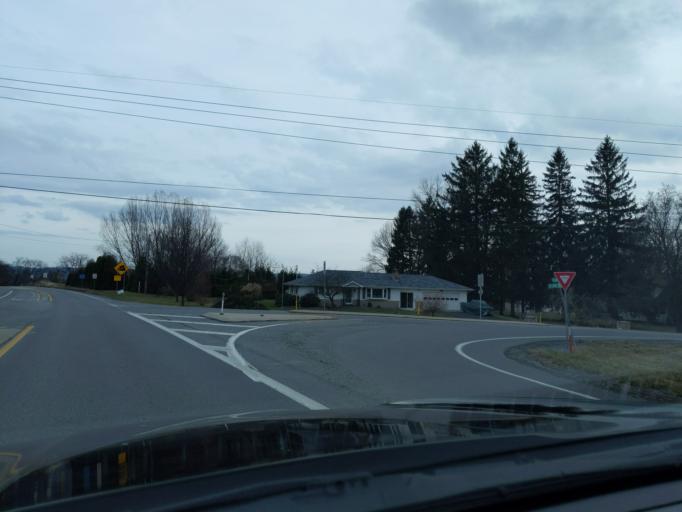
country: US
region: Pennsylvania
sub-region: Blair County
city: Lakemont
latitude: 40.4618
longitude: -78.3757
